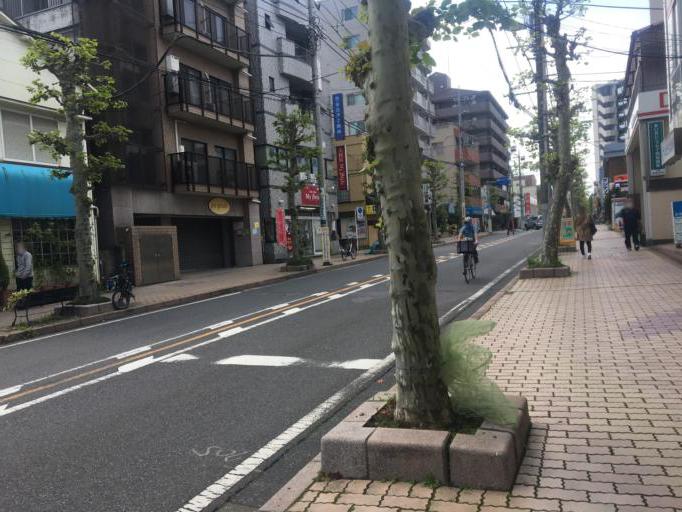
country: JP
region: Saitama
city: Wako
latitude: 35.7861
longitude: 139.6097
